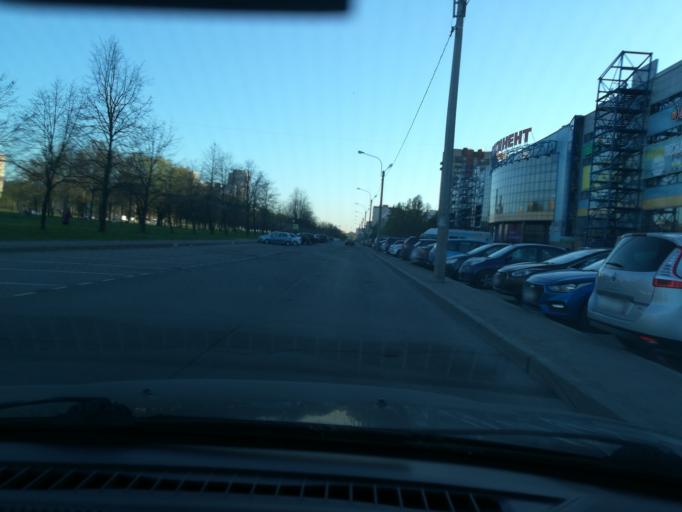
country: RU
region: St.-Petersburg
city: Dachnoye
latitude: 59.8590
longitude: 30.2504
